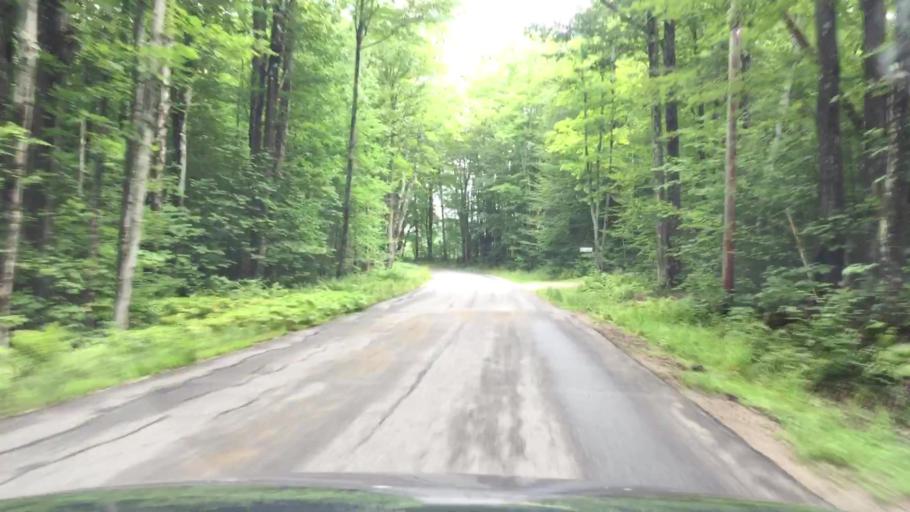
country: US
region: New Hampshire
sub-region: Carroll County
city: Sandwich
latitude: 43.7994
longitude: -71.4732
